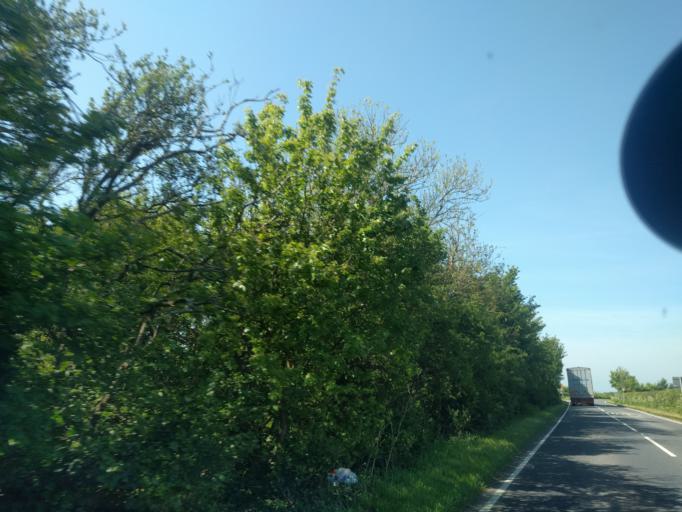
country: GB
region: England
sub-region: Somerset
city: Ilchester
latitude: 51.0304
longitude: -2.7247
